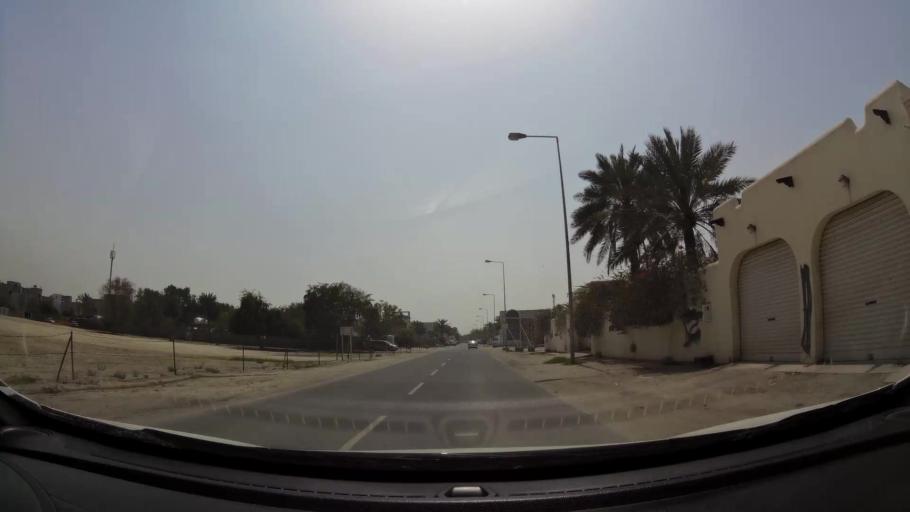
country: BH
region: Manama
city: Jidd Hafs
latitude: 26.2254
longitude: 50.4825
